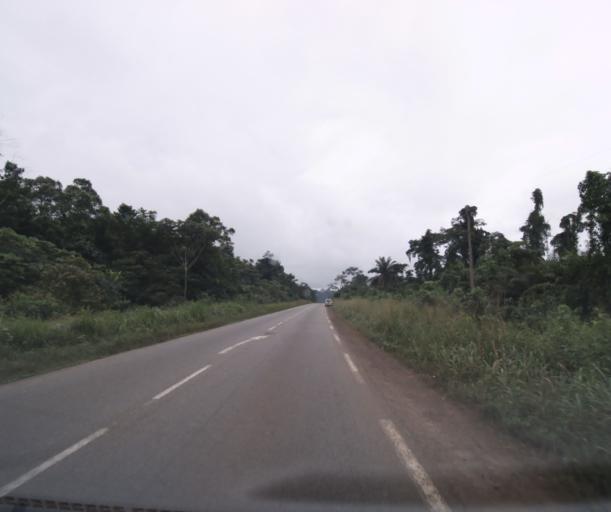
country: CM
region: Littoral
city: Edea
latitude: 3.8045
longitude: 10.2524
